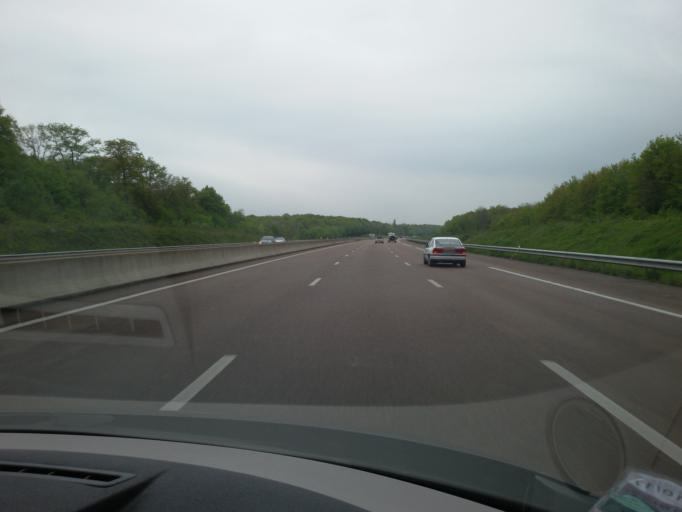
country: FR
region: Bourgogne
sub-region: Departement de la Cote-d'Or
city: Gevrey-Chambertin
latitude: 47.1907
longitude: 4.9973
